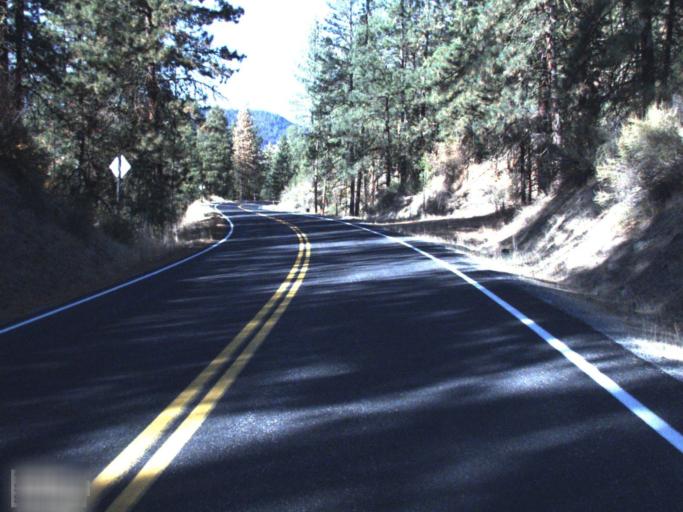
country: US
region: Washington
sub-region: Stevens County
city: Kettle Falls
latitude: 48.1789
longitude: -118.1679
